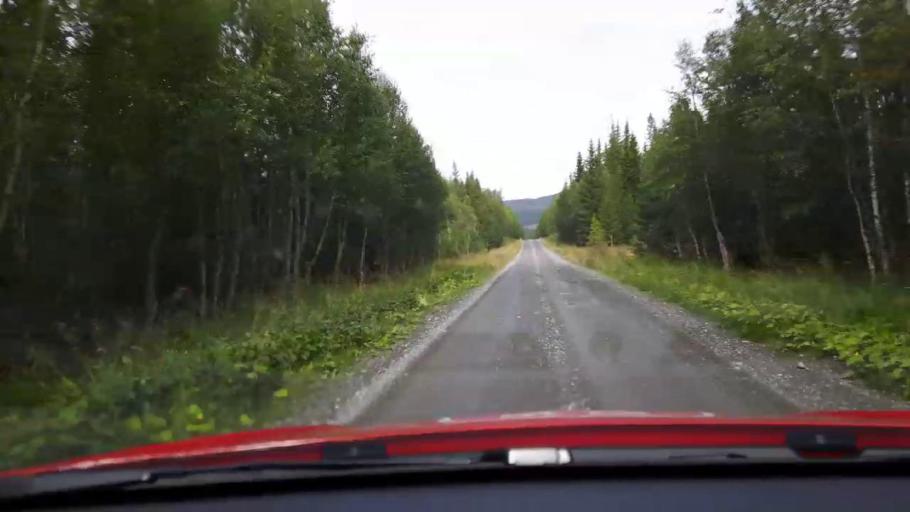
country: SE
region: Jaemtland
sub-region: Are Kommun
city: Are
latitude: 63.7870
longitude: 13.1051
